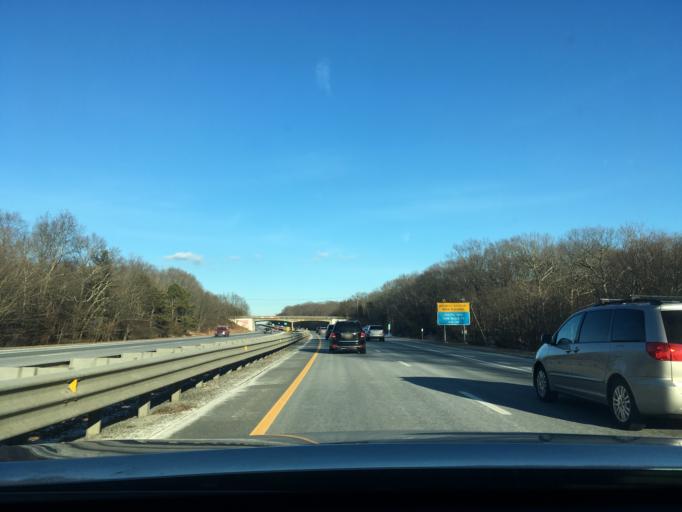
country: US
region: Rhode Island
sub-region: Kent County
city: West Warwick
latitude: 41.6600
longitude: -71.5309
